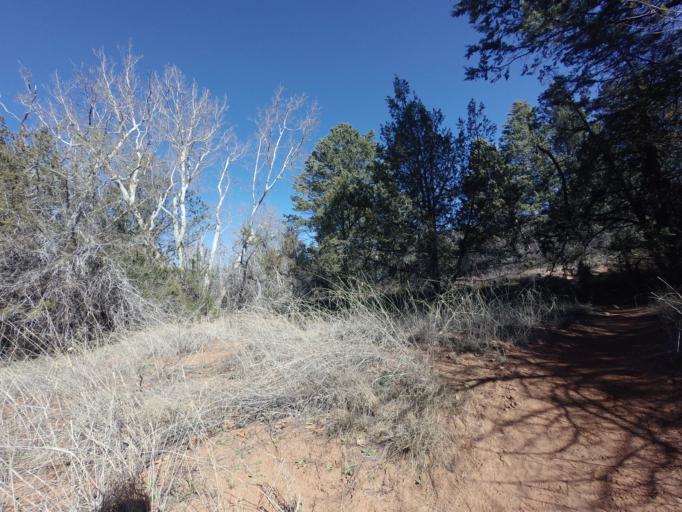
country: US
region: Arizona
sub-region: Yavapai County
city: West Sedona
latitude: 34.8232
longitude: -111.8028
